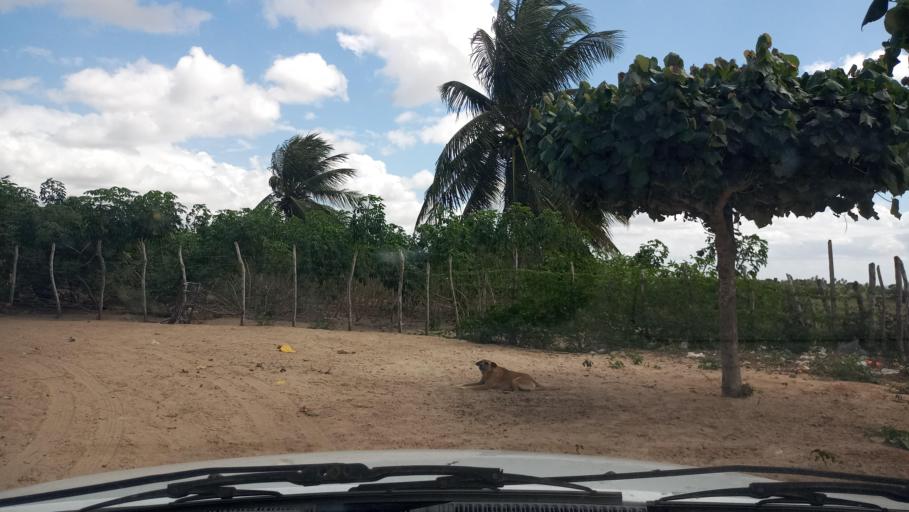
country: BR
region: Rio Grande do Norte
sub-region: Brejinho
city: Brejinho
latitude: -6.1915
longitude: -35.3668
